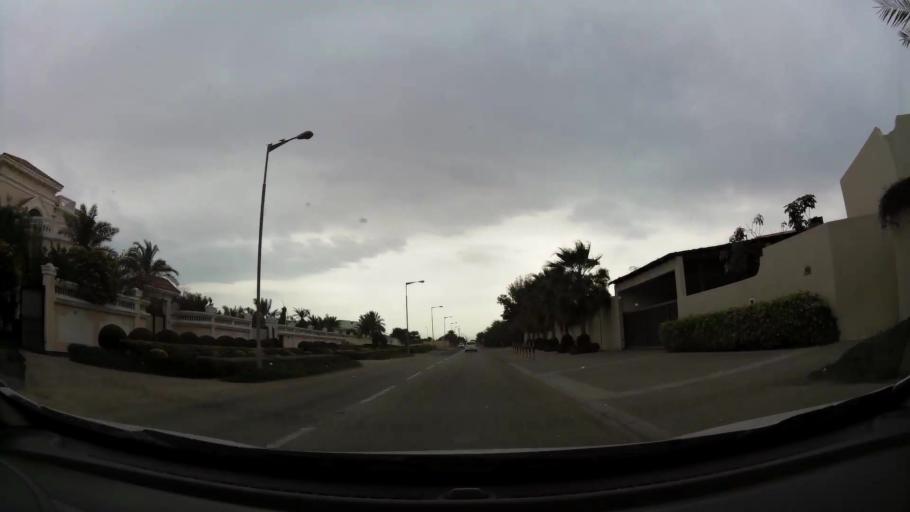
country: BH
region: Central Governorate
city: Madinat Hamad
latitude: 26.1513
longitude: 50.4644
